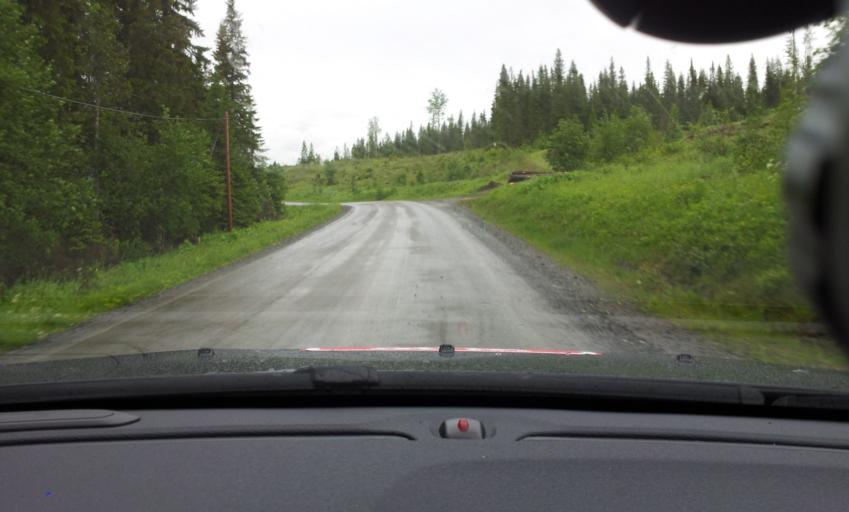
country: SE
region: Jaemtland
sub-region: Are Kommun
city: Are
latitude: 63.4241
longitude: 12.8182
